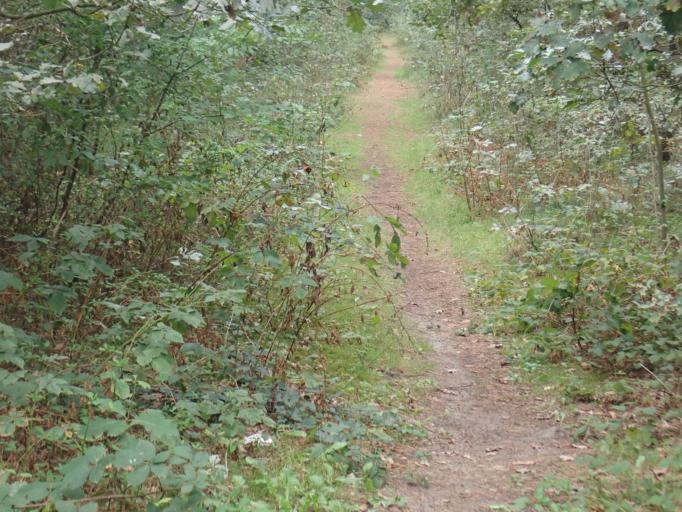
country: BE
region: Flanders
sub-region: Provincie Antwerpen
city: Lille
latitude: 51.2736
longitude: 4.8206
